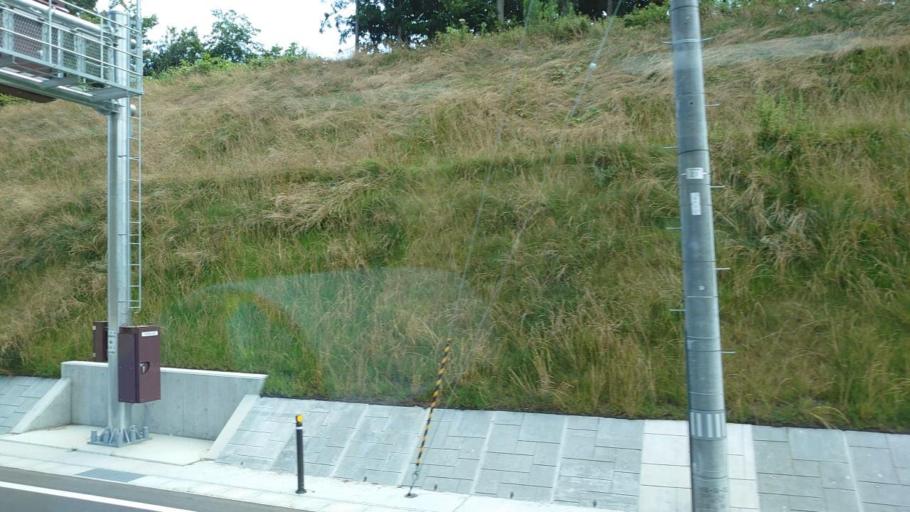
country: JP
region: Iwate
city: Ofunato
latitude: 38.8693
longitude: 141.6068
